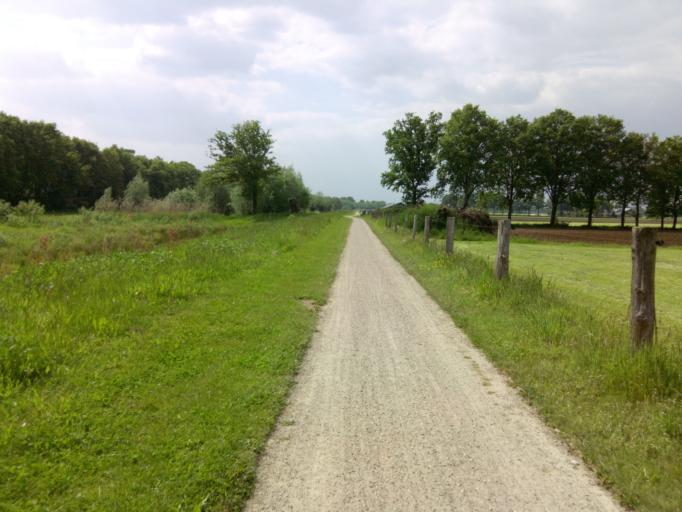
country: NL
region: Gelderland
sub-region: Oost Gelre
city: Lichtenvoorde
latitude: 52.0481
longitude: 6.5401
